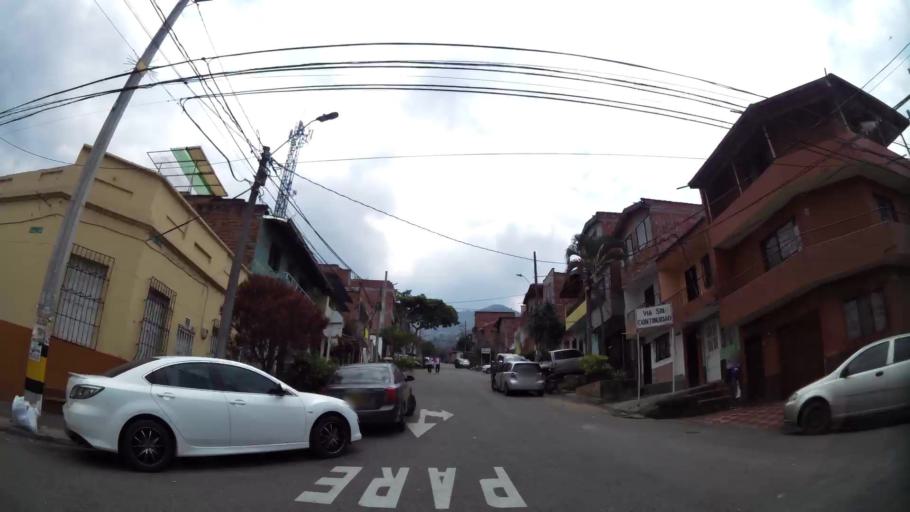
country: CO
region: Antioquia
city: Medellin
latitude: 6.2703
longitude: -75.5556
